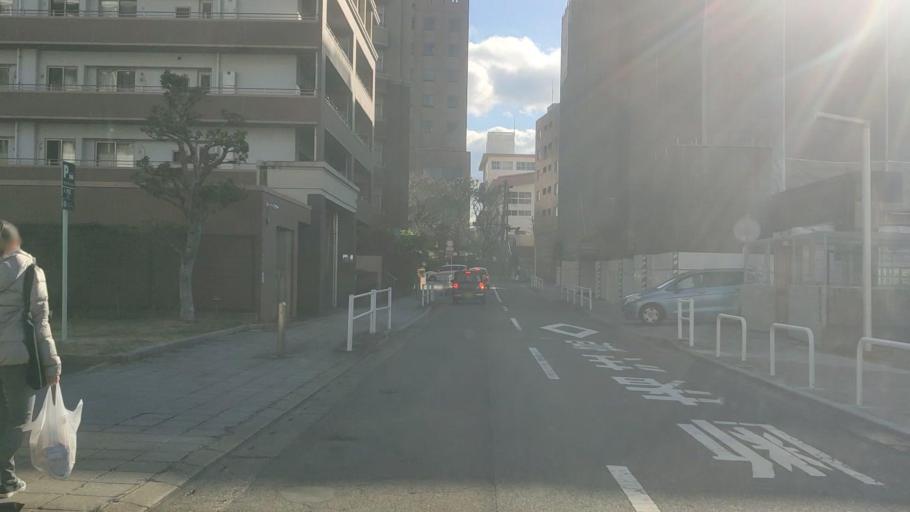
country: JP
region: Fukuoka
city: Fukuoka-shi
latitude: 33.5735
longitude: 130.3655
